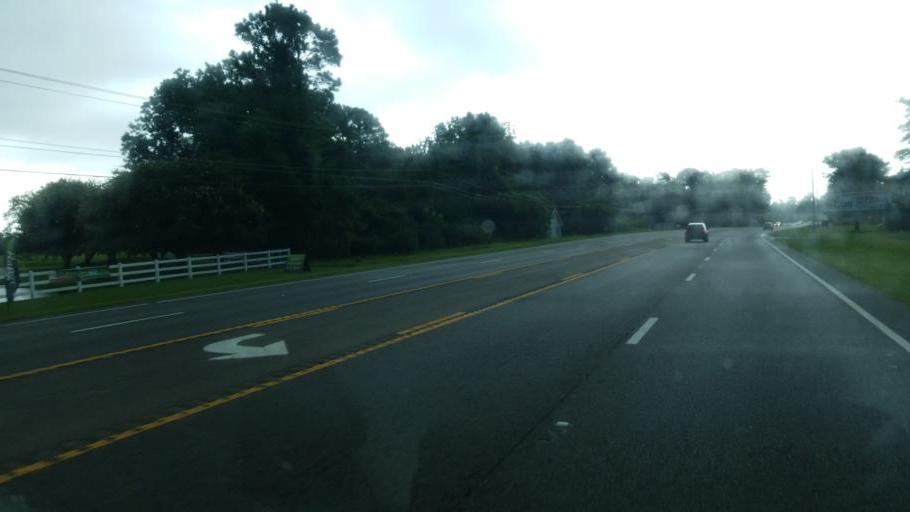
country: US
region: North Carolina
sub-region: Dare County
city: Southern Shores
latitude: 36.1154
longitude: -75.8288
